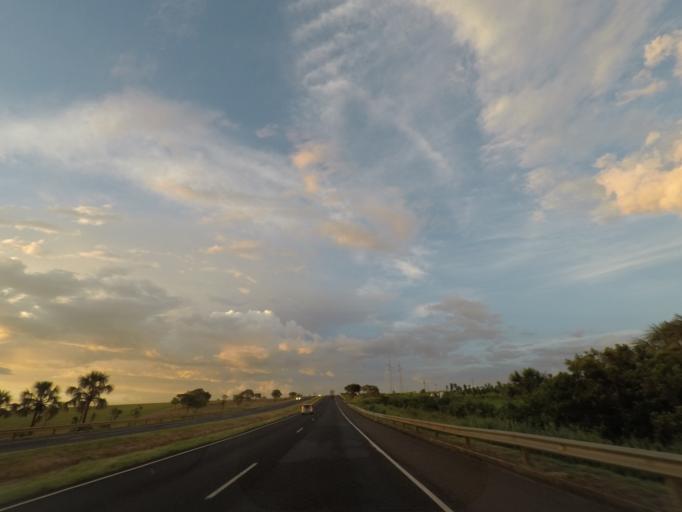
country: BR
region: Minas Gerais
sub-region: Uberaba
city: Uberaba
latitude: -19.6554
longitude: -48.0040
